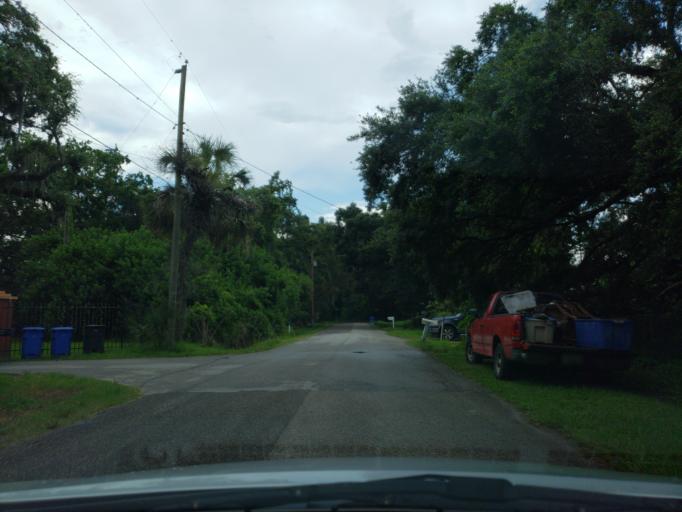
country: US
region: Florida
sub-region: Hillsborough County
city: Palm River-Clair Mel
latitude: 27.9324
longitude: -82.4076
